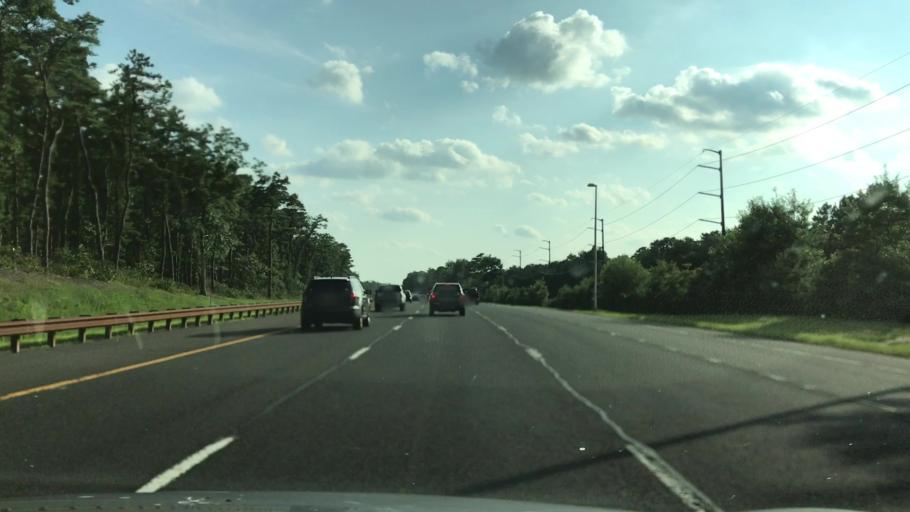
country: US
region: New Jersey
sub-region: Ocean County
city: Tuckerton
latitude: 39.6522
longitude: -74.3491
